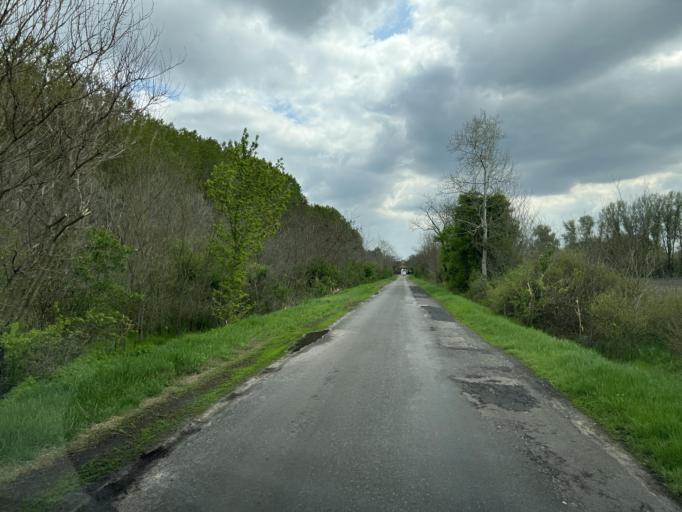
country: HU
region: Pest
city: Orkeny
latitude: 47.0459
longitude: 19.3398
